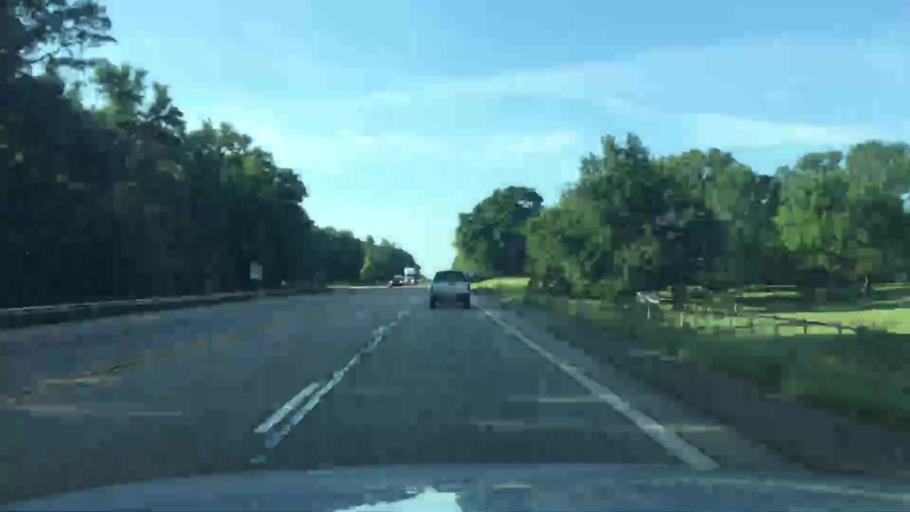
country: US
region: Michigan
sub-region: Jackson County
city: Vandercook Lake
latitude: 42.0904
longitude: -84.3639
